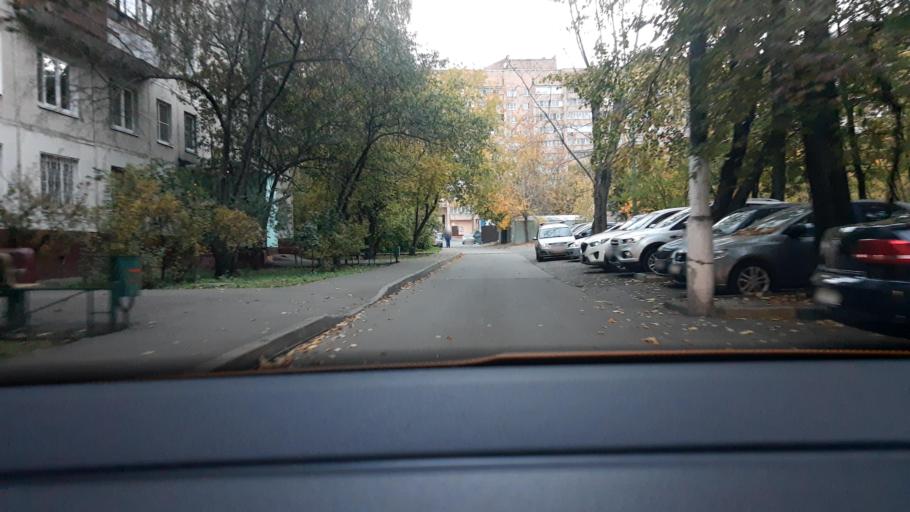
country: RU
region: Moscow
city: Otradnoye
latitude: 55.8702
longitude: 37.5969
